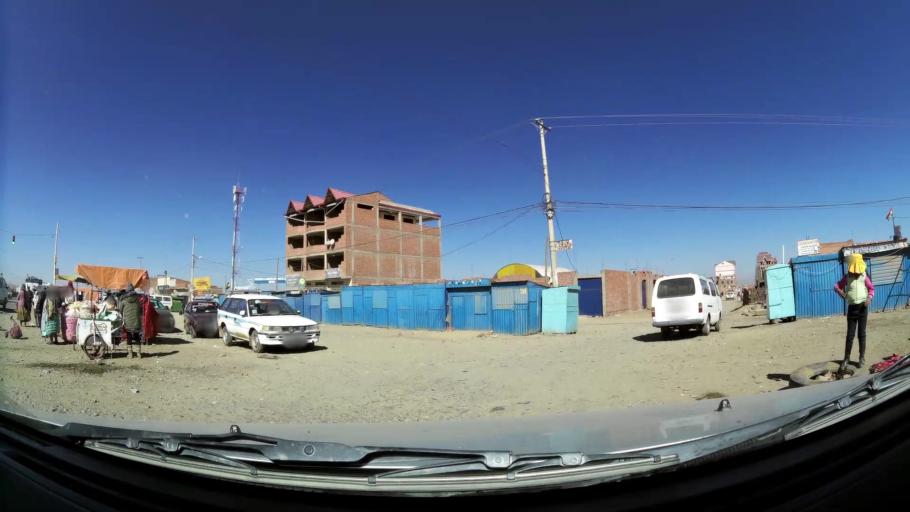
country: BO
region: La Paz
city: La Paz
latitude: -16.6185
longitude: -68.1826
